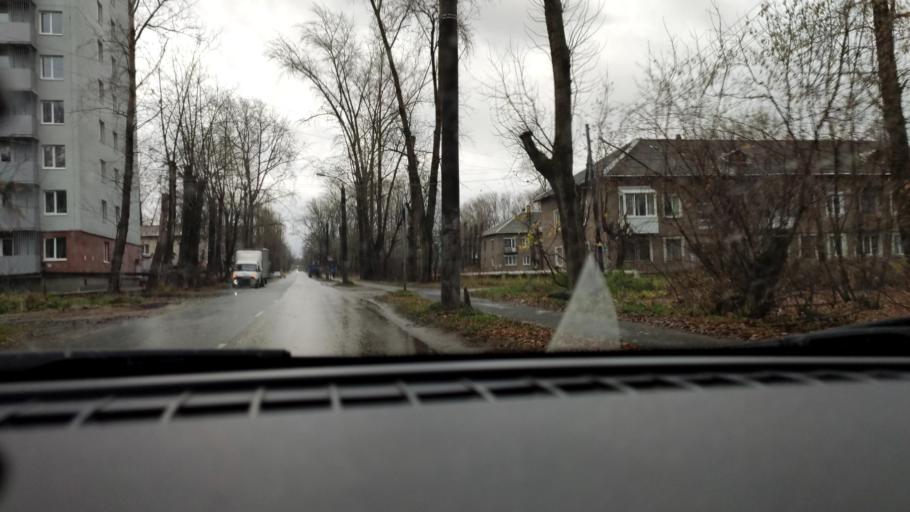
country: RU
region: Perm
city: Perm
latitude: 58.0942
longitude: 56.3763
